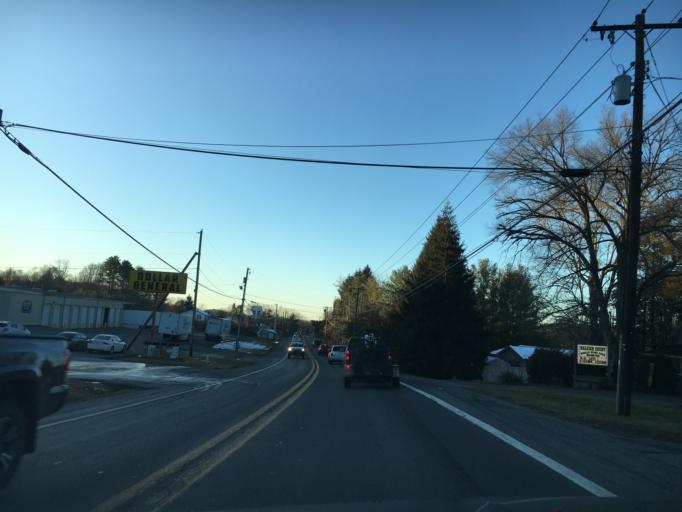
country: US
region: West Virginia
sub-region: Raleigh County
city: Daniels
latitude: 37.7408
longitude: -81.1168
